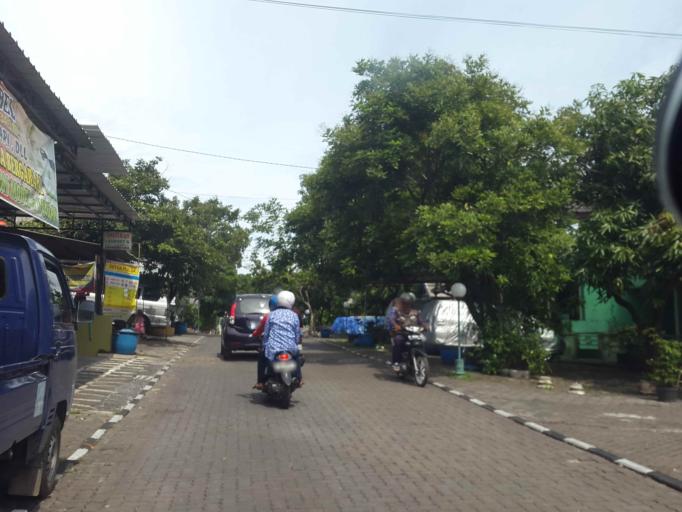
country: ID
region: Central Java
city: Semarang
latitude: -7.0093
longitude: 110.3719
